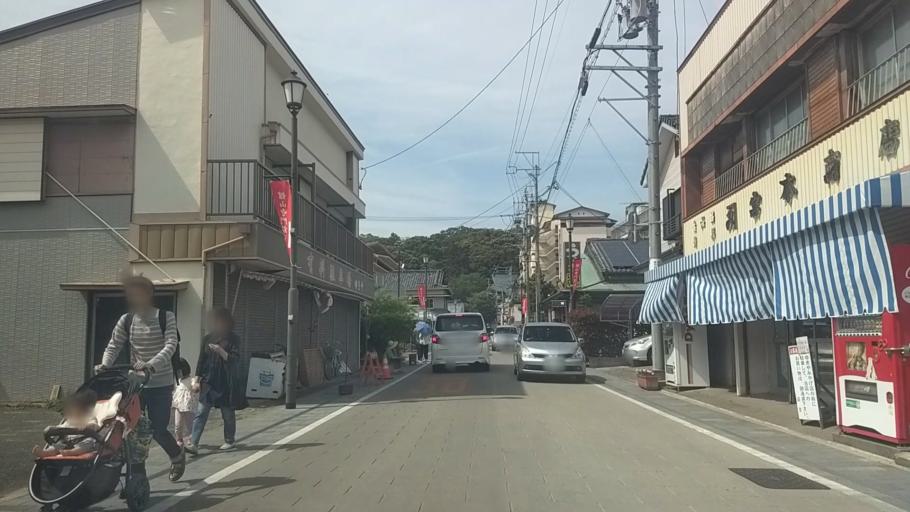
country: JP
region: Shizuoka
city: Kosai-shi
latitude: 34.7660
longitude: 137.6134
